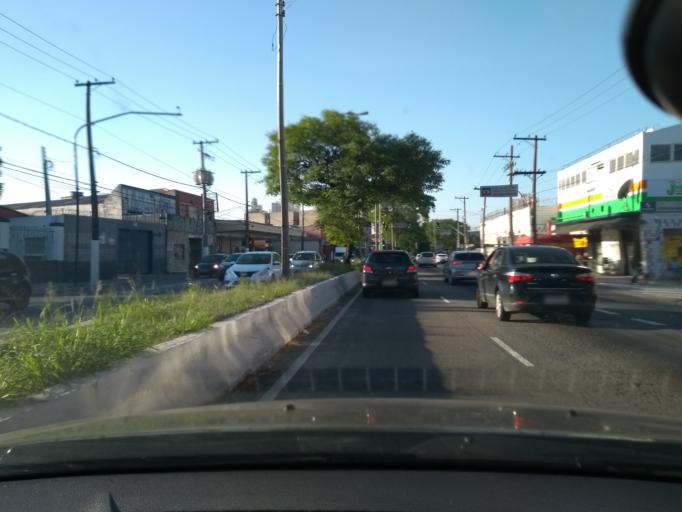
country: BR
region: Sao Paulo
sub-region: Sao Caetano Do Sul
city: Sao Caetano do Sul
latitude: -23.6179
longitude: -46.6017
